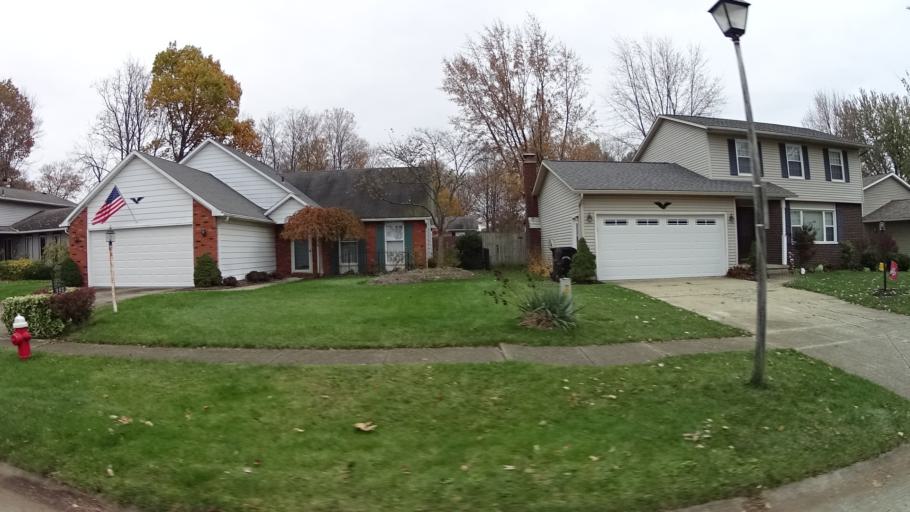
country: US
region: Ohio
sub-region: Lorain County
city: Sheffield
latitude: 41.4170
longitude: -82.0879
